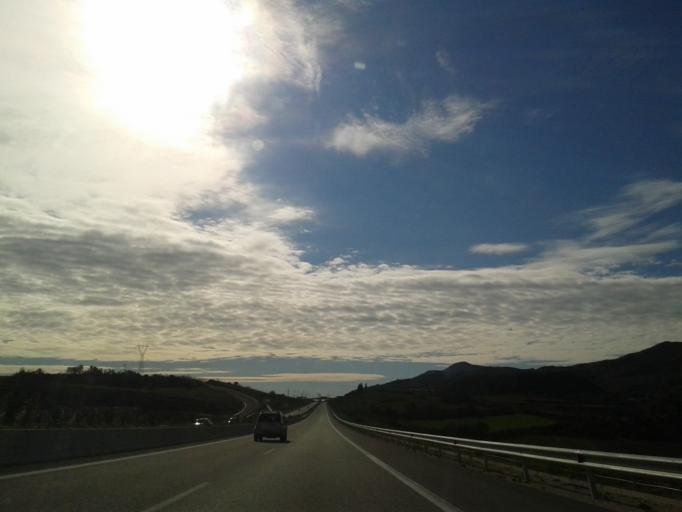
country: GR
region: West Greece
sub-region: Nomos Aitolias kai Akarnanias
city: Fitiai
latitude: 38.7112
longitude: 21.2088
